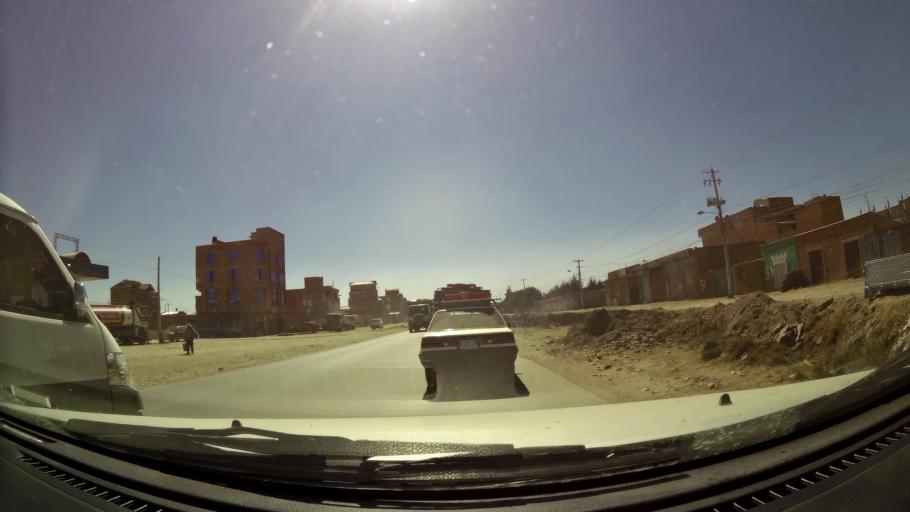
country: BO
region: La Paz
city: La Paz
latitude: -16.5496
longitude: -68.2045
